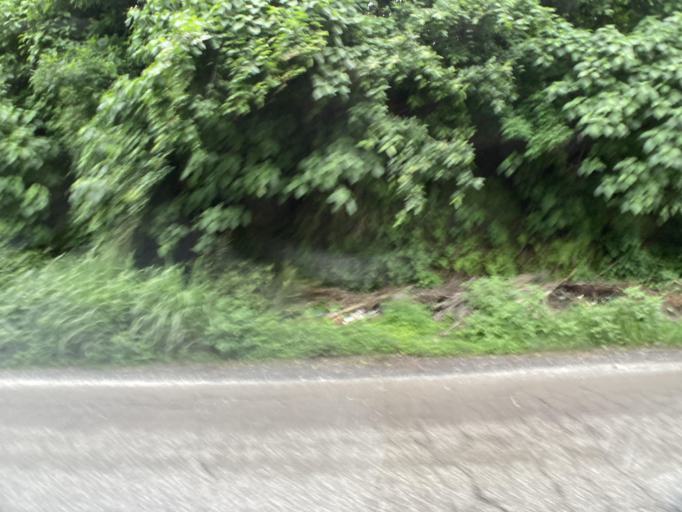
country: GT
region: Guatemala
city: Villa Canales
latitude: 14.4373
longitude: -90.5352
